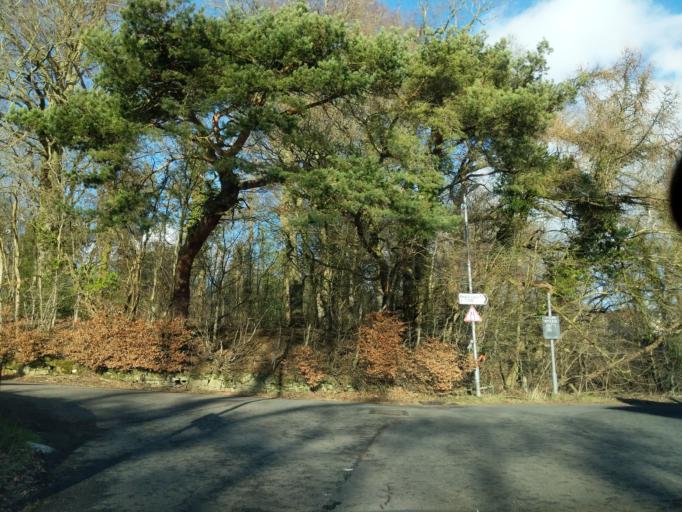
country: GB
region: Scotland
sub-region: South Lanarkshire
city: Carluke
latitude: 55.7090
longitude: -3.8460
